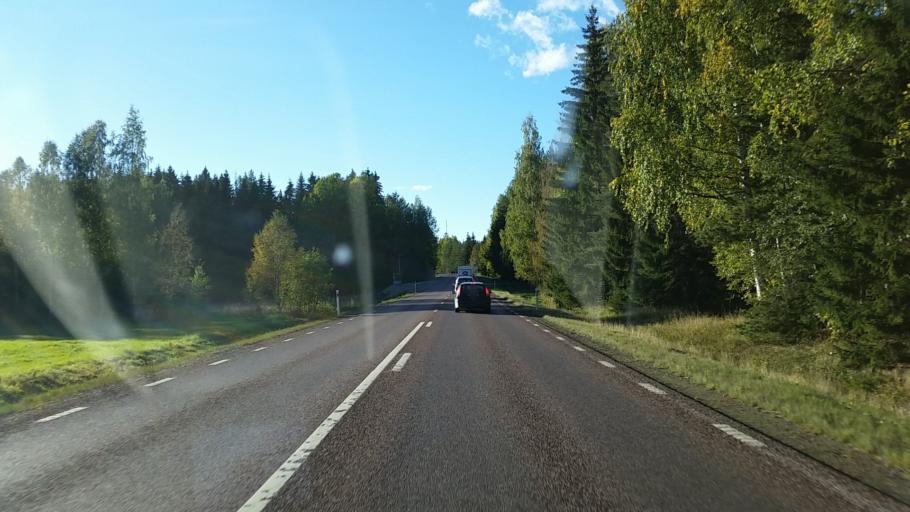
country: SE
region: Gaevleborg
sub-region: Hudiksvalls Kommun
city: Delsbo
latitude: 61.8030
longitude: 16.4714
